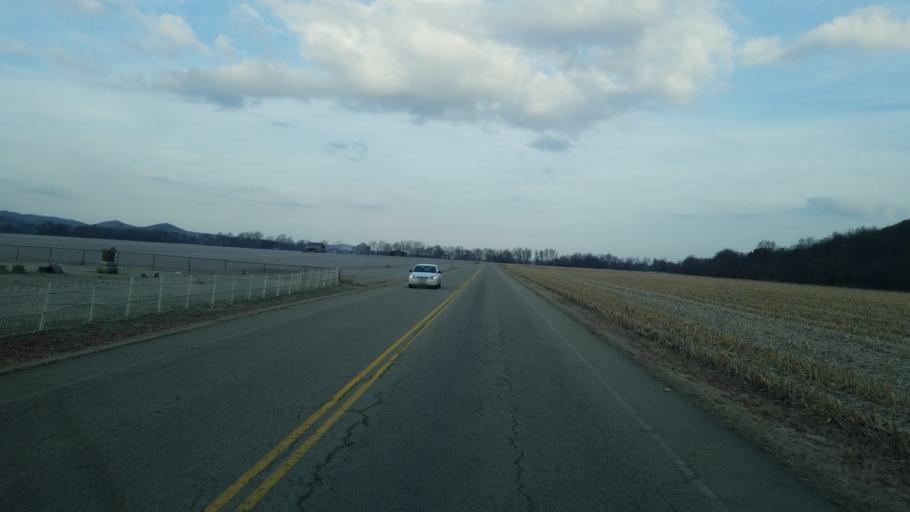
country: US
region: Ohio
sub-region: Pike County
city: Waverly
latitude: 39.2223
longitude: -82.8495
